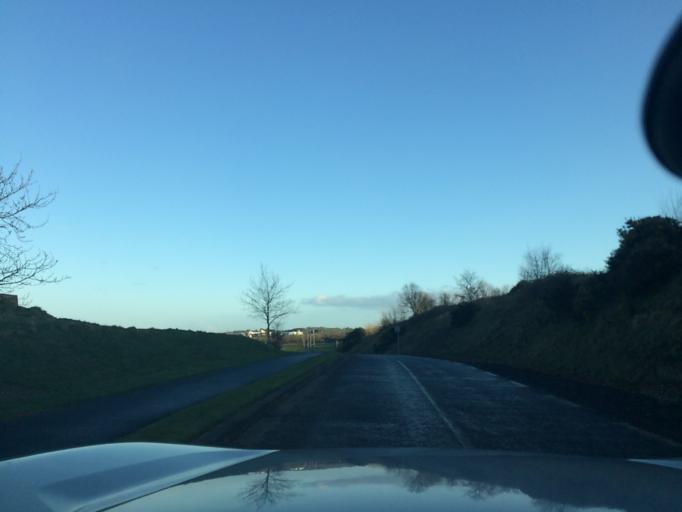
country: IE
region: Munster
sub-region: Waterford
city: Waterford
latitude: 52.2530
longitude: -7.1847
